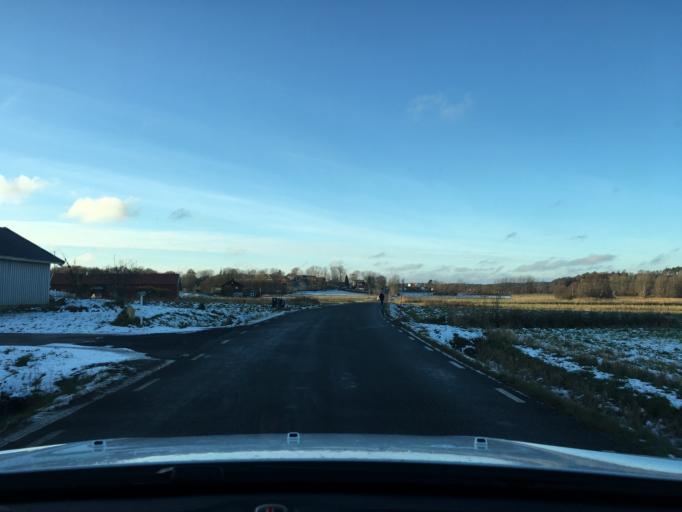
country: SE
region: Vaestra Goetaland
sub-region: Tjorns Kommun
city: Myggenas
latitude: 58.0470
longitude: 11.7233
